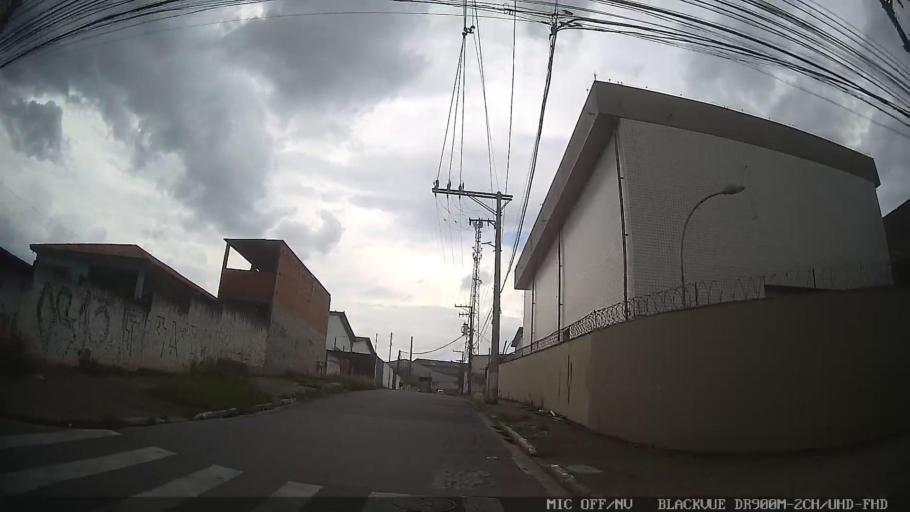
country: BR
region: Sao Paulo
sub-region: Itaquaquecetuba
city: Itaquaquecetuba
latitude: -23.4638
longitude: -46.3266
